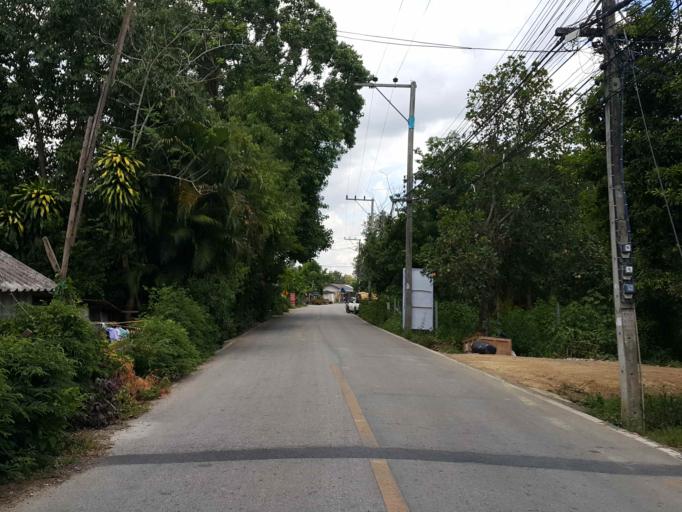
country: TH
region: Chiang Mai
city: Saraphi
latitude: 18.7382
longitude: 98.9964
